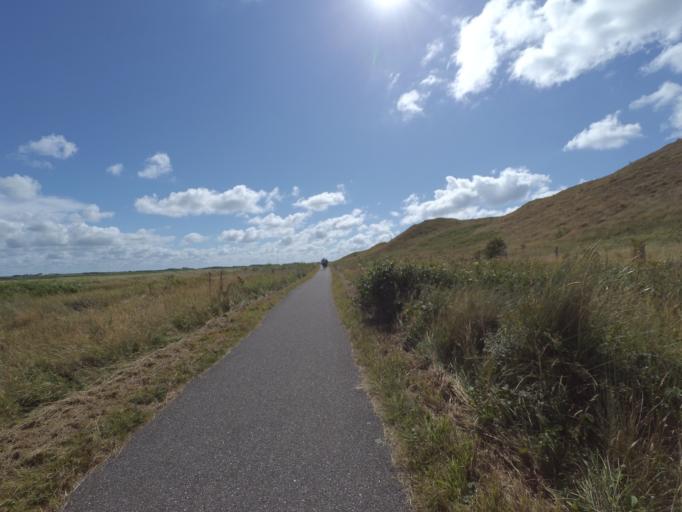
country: NL
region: North Holland
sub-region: Gemeente Texel
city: Den Burg
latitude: 53.1218
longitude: 4.8060
